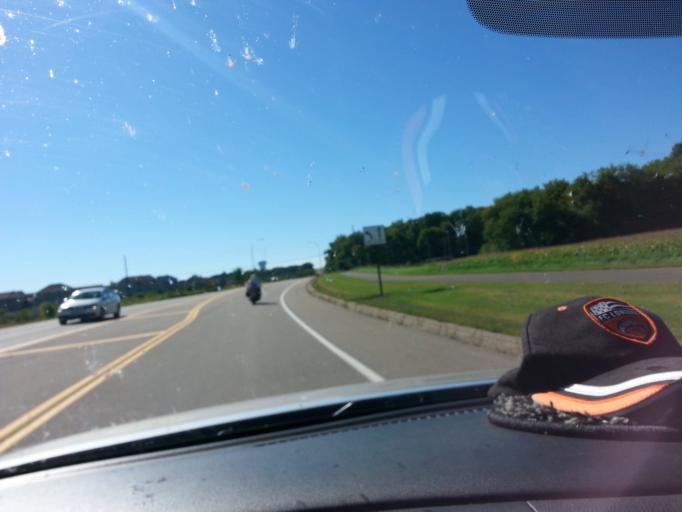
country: US
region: Minnesota
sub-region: Dakota County
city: Farmington
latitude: 44.6670
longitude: -93.1538
